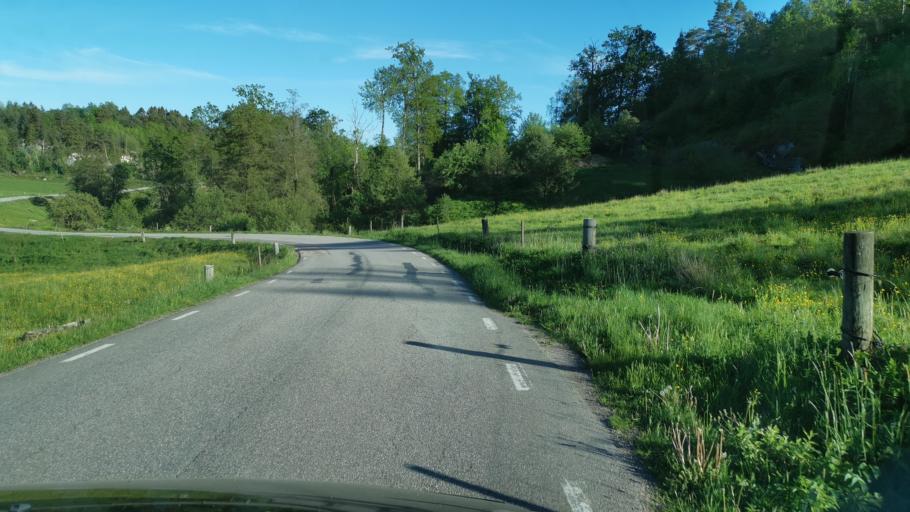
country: SE
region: Vaestra Goetaland
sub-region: Orust
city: Henan
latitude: 58.2713
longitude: 11.6005
